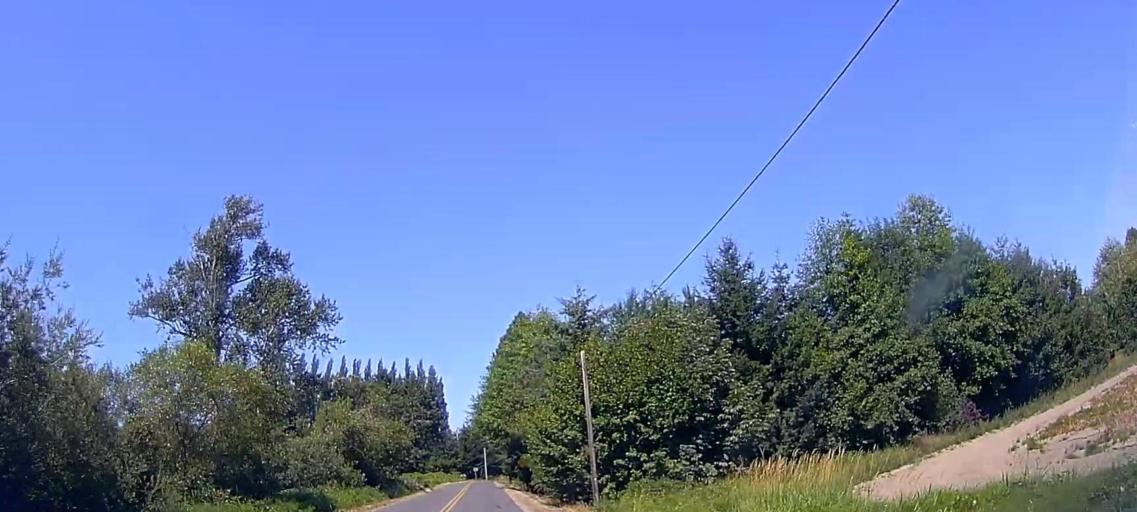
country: US
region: Washington
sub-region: Skagit County
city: Burlington
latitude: 48.4850
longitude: -122.2966
